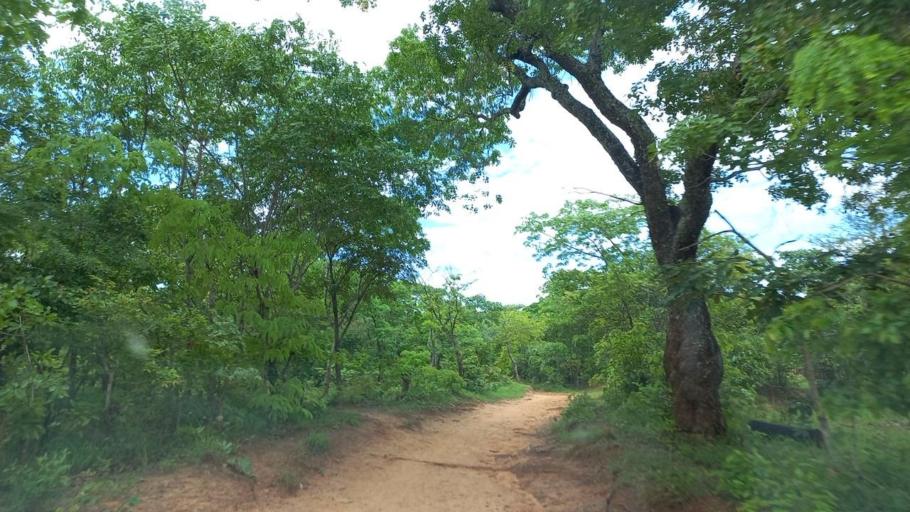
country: ZM
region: North-Western
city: Kabompo
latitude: -13.6085
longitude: 24.2494
